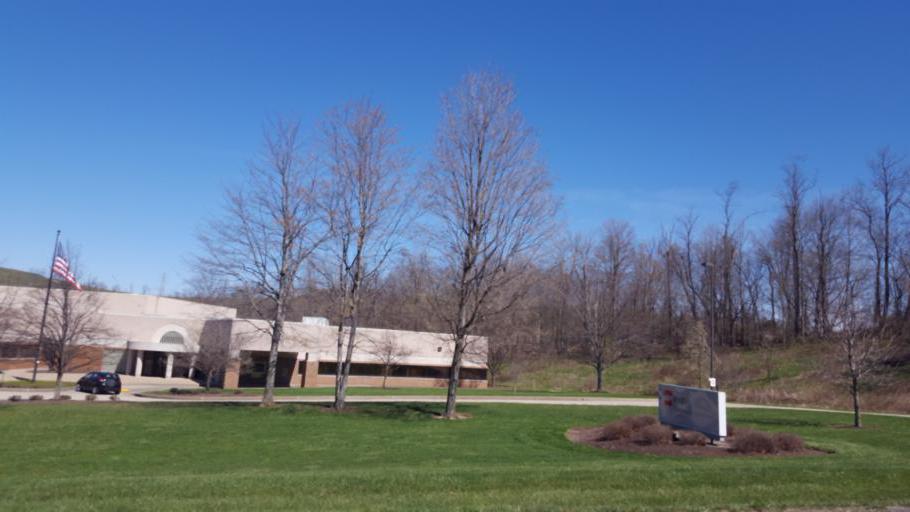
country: US
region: Ohio
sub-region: Belmont County
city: Saint Clairsville
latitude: 40.0757
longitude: -80.9322
